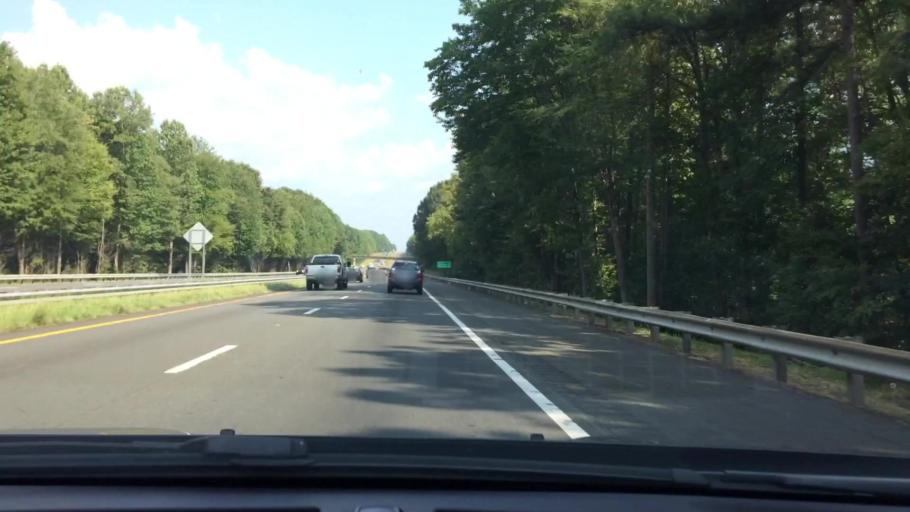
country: US
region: North Carolina
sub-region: Orange County
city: Hillsborough
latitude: 36.0558
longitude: -79.0729
